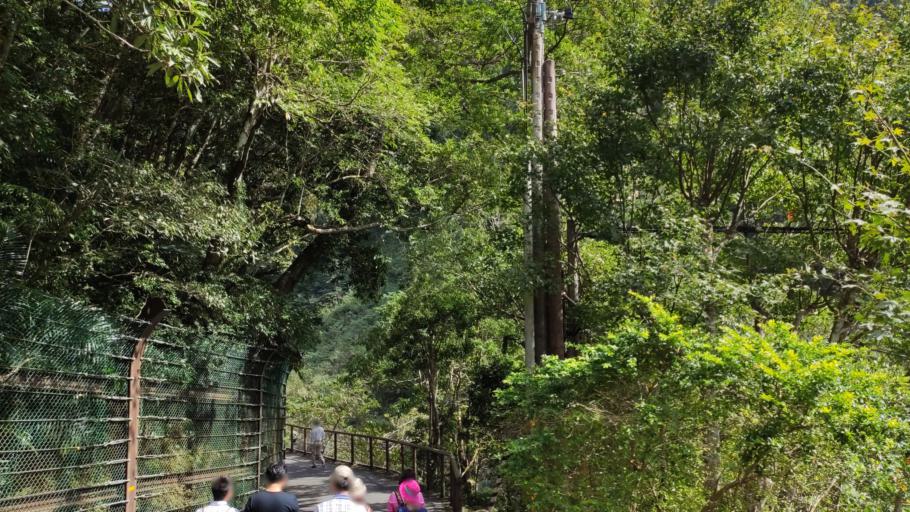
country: TW
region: Taiwan
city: Daxi
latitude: 24.8309
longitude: 121.4446
